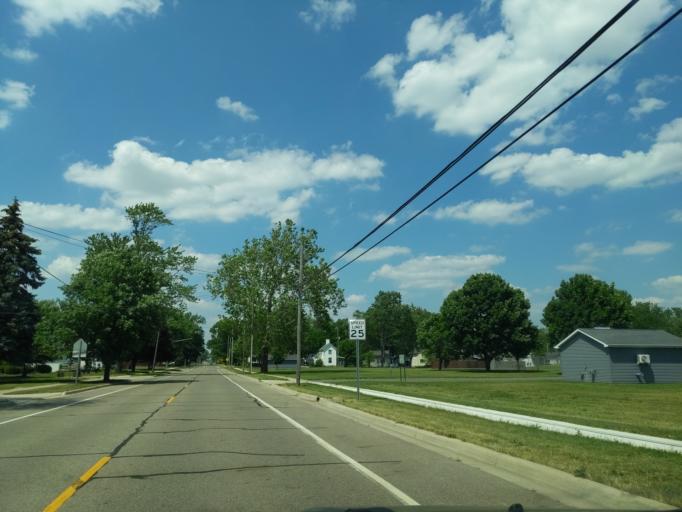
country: US
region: Michigan
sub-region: Clinton County
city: Saint Johns
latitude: 43.0094
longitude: -84.5626
